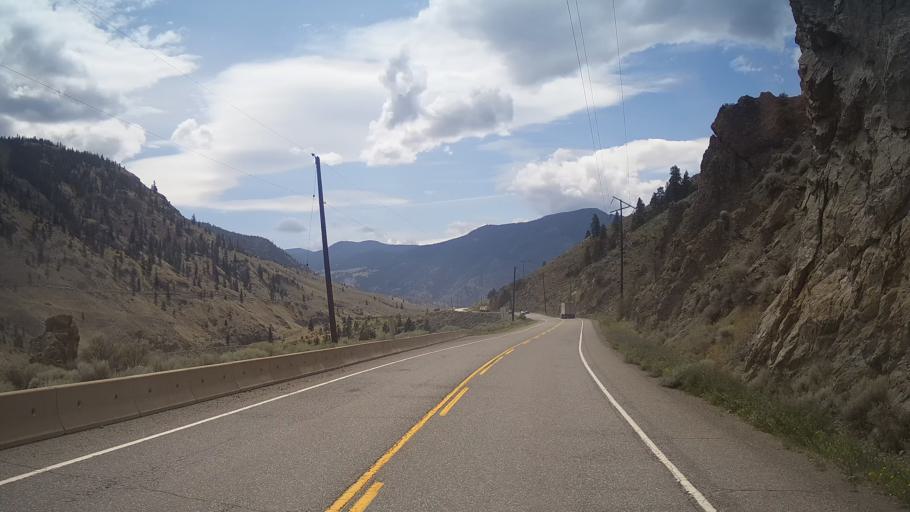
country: CA
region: British Columbia
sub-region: Thompson-Nicola Regional District
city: Ashcroft
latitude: 50.4669
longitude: -121.3004
